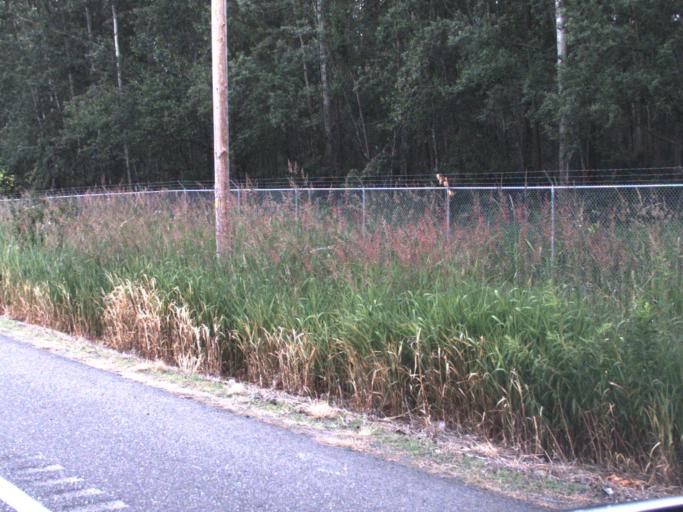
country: US
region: Washington
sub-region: Whatcom County
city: Birch Bay
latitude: 48.8920
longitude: -122.7139
